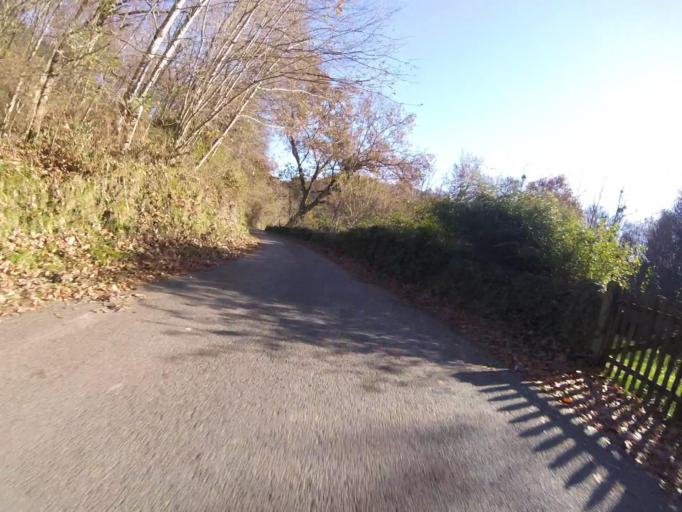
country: ES
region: Navarre
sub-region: Provincia de Navarra
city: Bera
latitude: 43.2883
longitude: -1.6465
